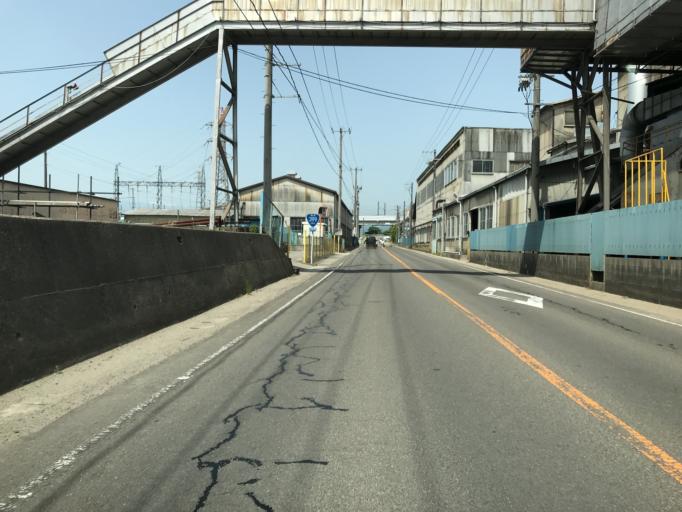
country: JP
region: Fukushima
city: Hobaramachi
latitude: 37.8217
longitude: 140.4961
